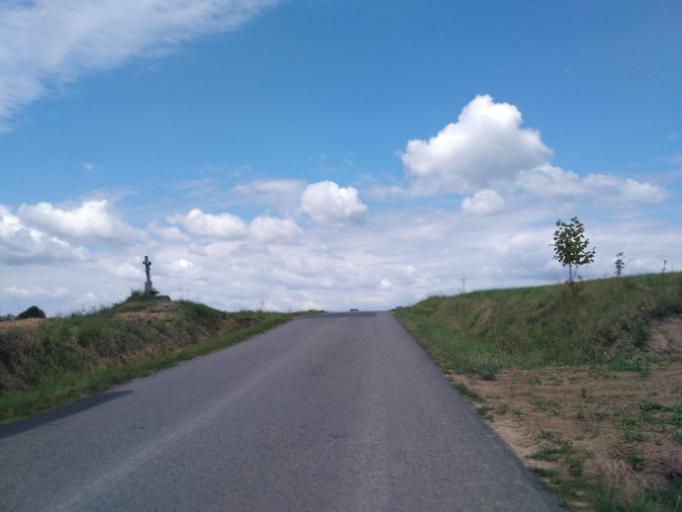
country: PL
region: Subcarpathian Voivodeship
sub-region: Powiat rzeszowski
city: Hyzne
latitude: 49.9141
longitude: 22.2159
